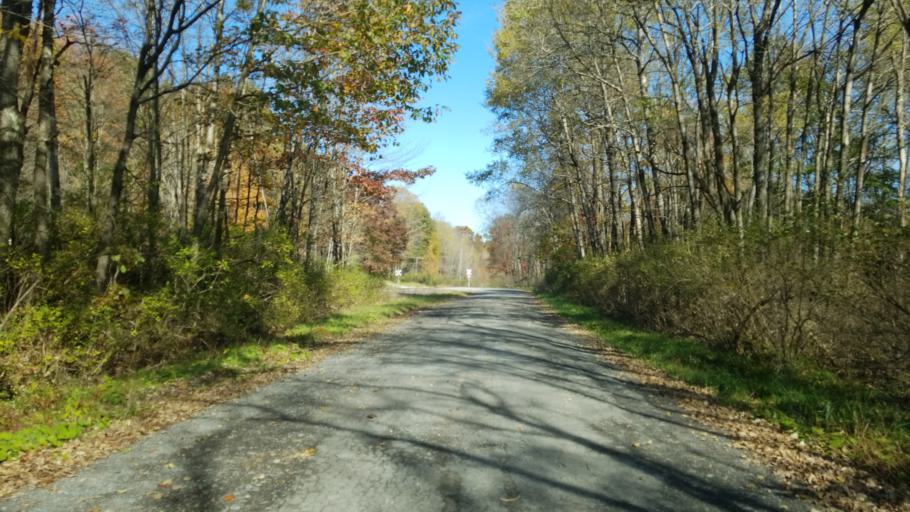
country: US
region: Pennsylvania
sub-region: Jefferson County
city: Falls Creek
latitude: 41.1746
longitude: -78.7850
